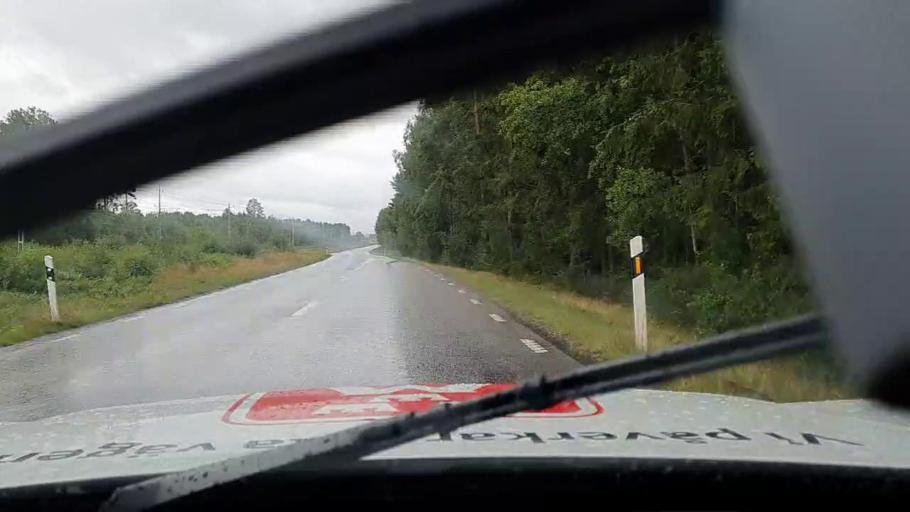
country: SE
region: Vaestra Goetaland
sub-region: Toreboda Kommun
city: Toereboda
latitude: 58.6648
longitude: 14.0908
